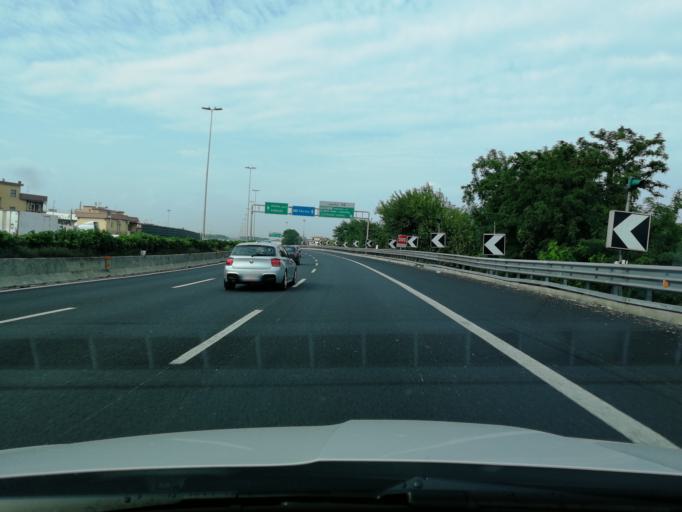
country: IT
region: Latium
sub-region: Citta metropolitana di Roma Capitale
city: Setteville
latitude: 41.9151
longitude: 12.6156
